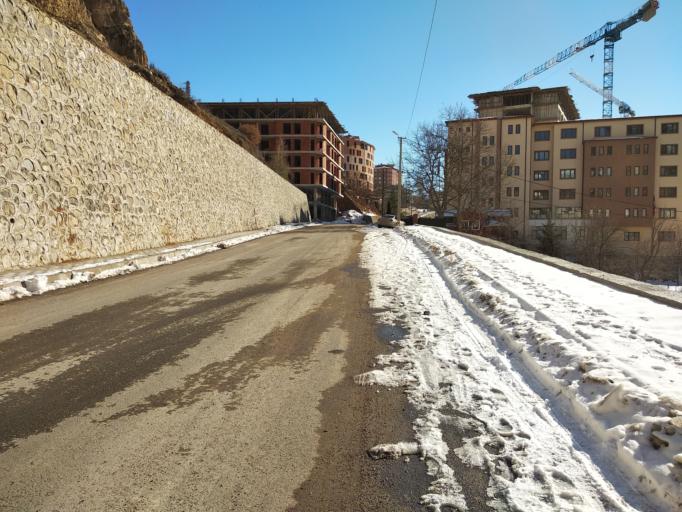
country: TR
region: Gumushane
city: Gumushkhane
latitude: 40.4390
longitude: 39.5053
